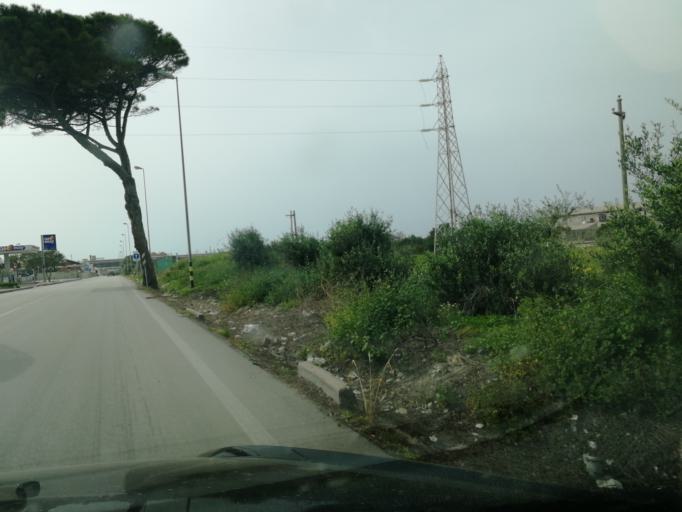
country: IT
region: Apulia
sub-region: Provincia di Barletta - Andria - Trani
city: Barletta
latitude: 41.3131
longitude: 16.3045
